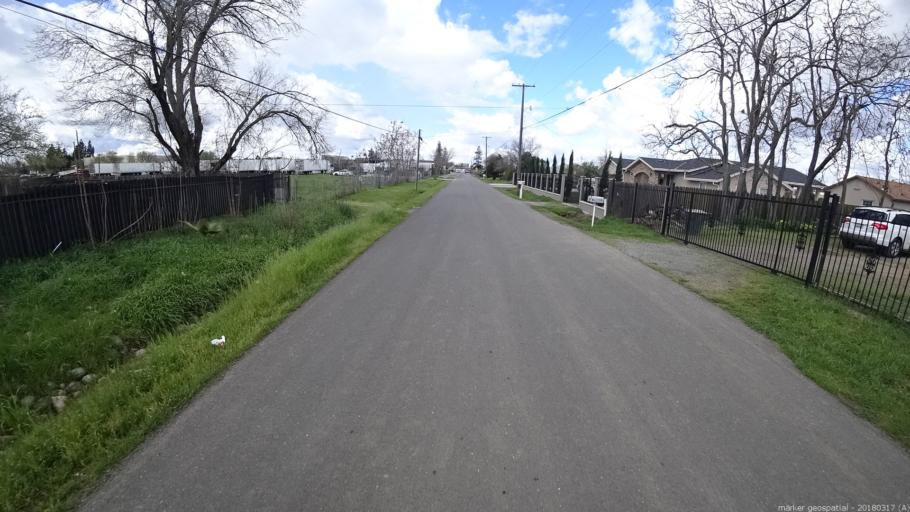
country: US
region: California
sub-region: Sacramento County
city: Florin
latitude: 38.4719
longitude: -121.4140
